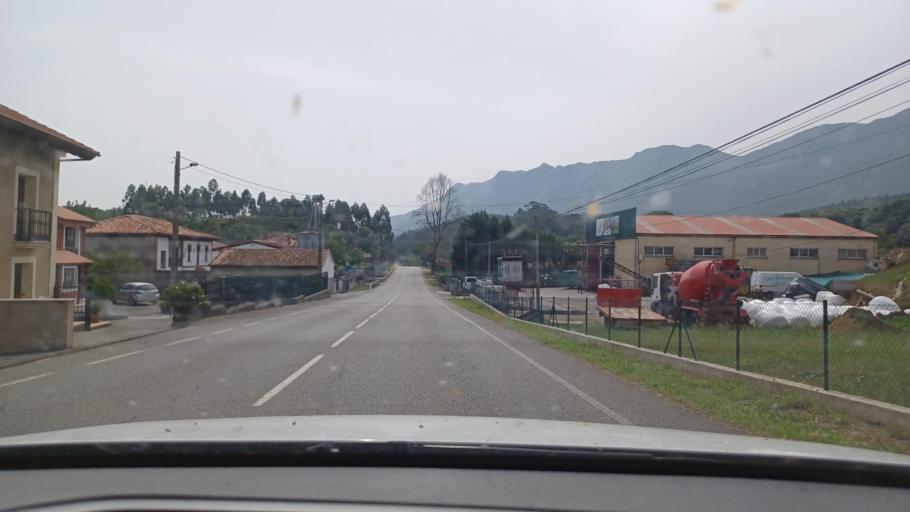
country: ES
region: Asturias
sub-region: Province of Asturias
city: Ribadesella
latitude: 43.4480
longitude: -5.0189
